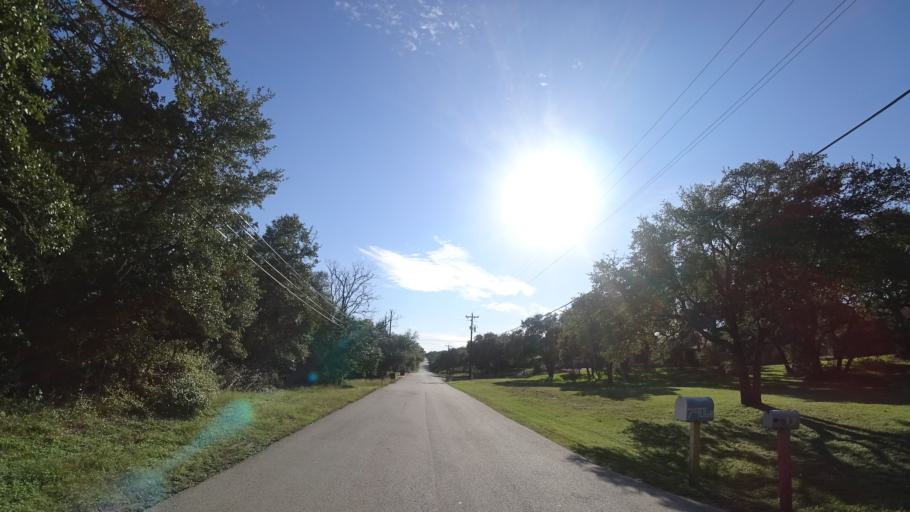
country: US
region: Texas
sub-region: Travis County
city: Barton Creek
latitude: 30.2391
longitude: -97.9087
